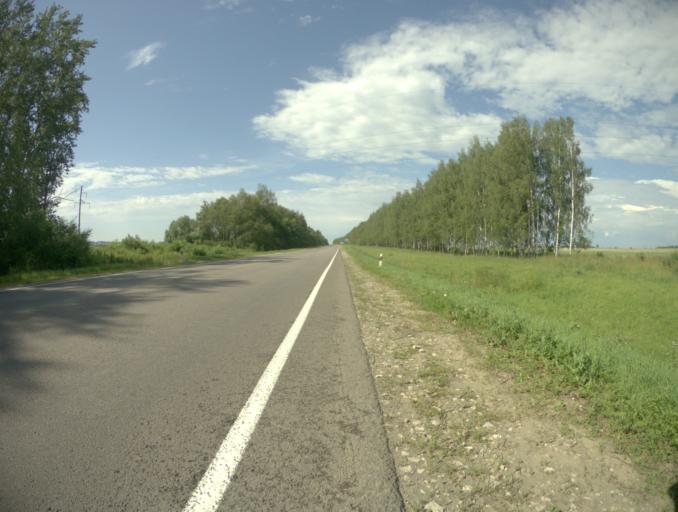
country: RU
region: Vladimir
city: Suzdal'
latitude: 56.3922
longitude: 40.4516
